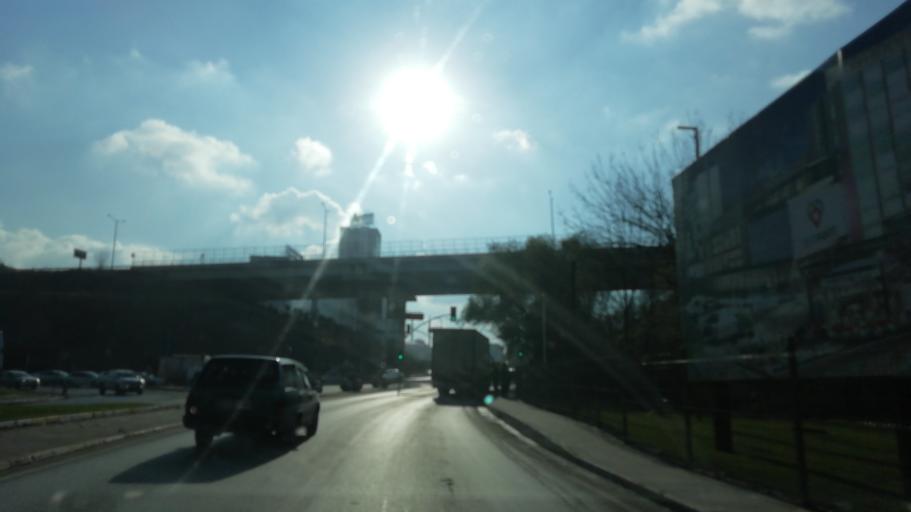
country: TR
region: Istanbul
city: Sultangazi
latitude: 41.0920
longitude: 28.9062
